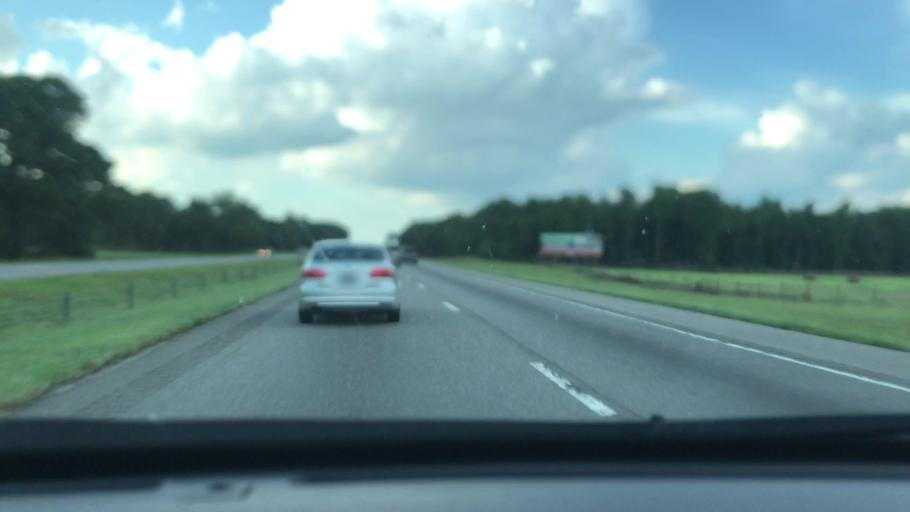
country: US
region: North Carolina
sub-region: Robeson County
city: Saint Pauls
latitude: 34.8677
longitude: -78.9640
